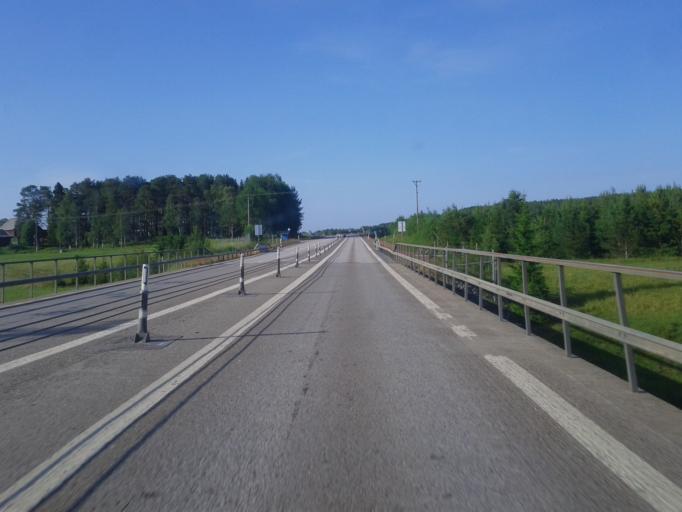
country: SE
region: Vaesterbotten
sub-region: Robertsfors Kommun
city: Robertsfors
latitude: 64.1298
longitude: 20.8893
